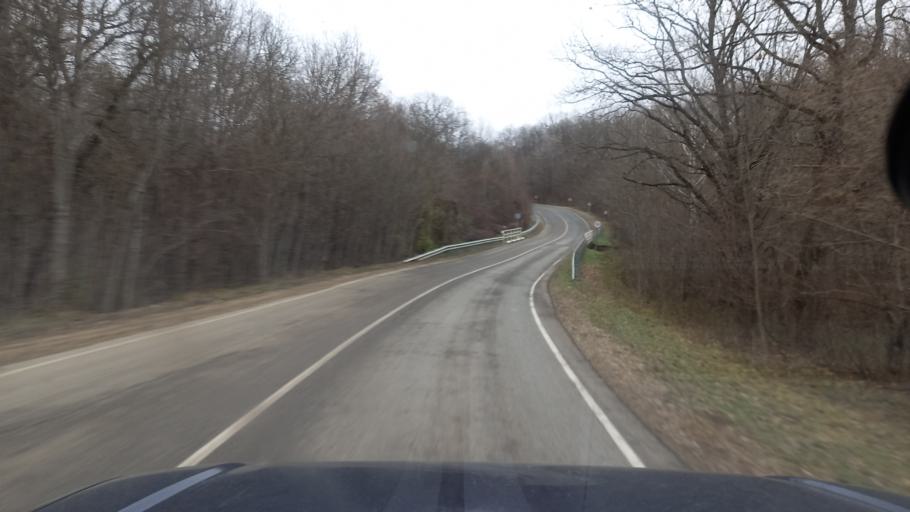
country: RU
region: Krasnodarskiy
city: Goryachiy Klyuch
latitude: 44.5446
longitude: 39.2719
